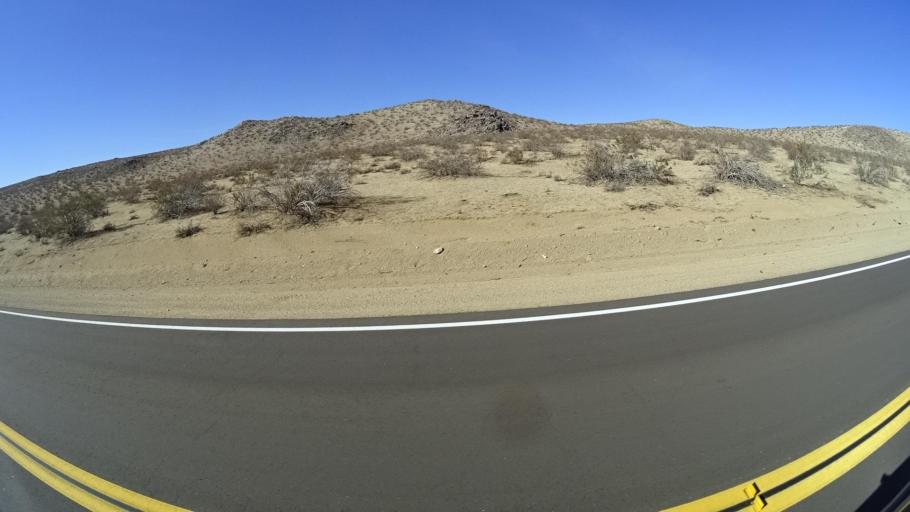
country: US
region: California
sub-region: Kern County
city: Ridgecrest
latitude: 35.5362
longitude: -117.5870
